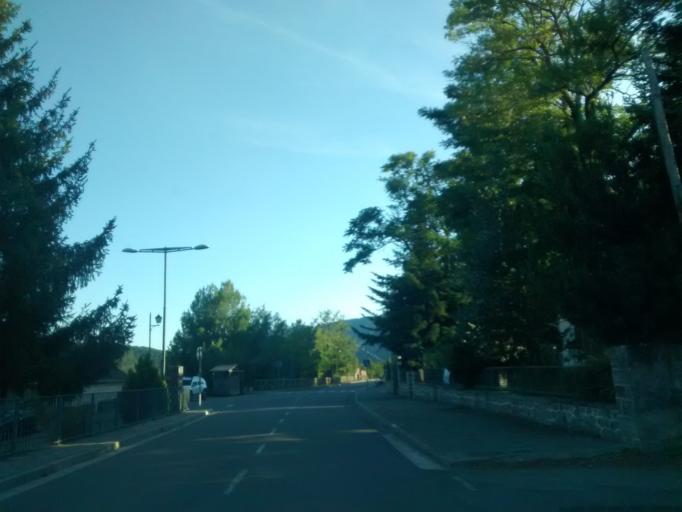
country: ES
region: Aragon
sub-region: Provincia de Huesca
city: Anso
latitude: 42.7368
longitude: -0.7517
